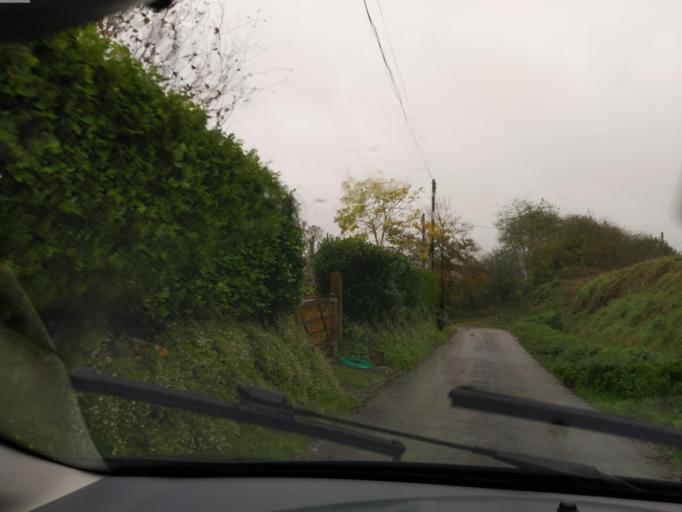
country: GB
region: England
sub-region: Devon
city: Bere Alston
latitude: 50.4685
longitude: -4.2374
